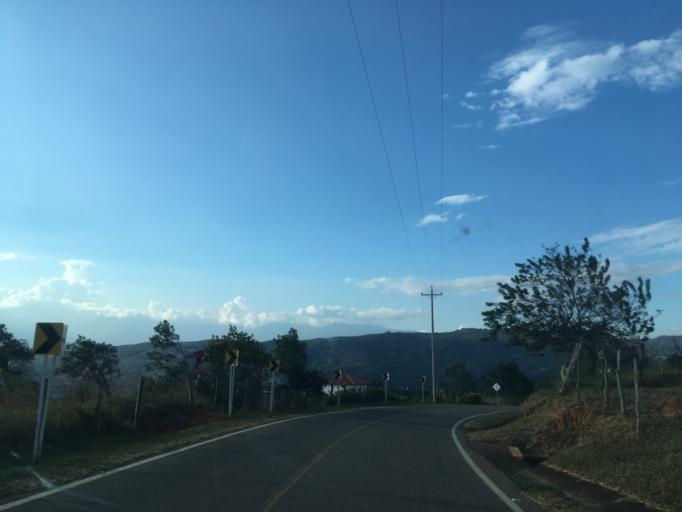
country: CO
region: Santander
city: Villanueva
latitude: 6.6338
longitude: -73.1803
